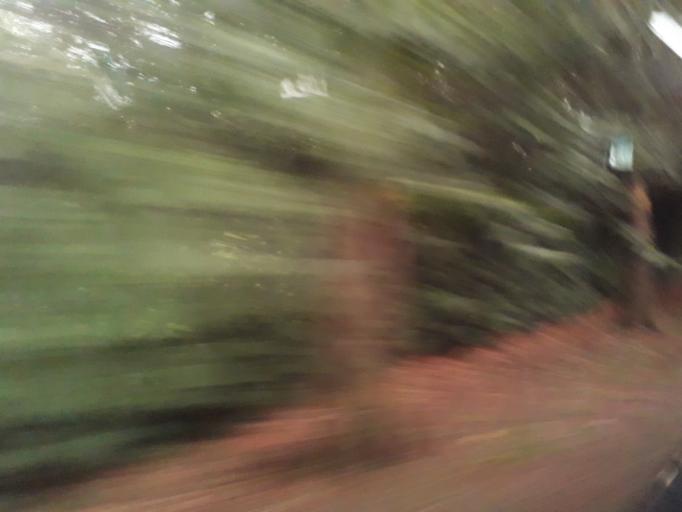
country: MY
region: Perak
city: Ipoh
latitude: 4.5994
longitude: 101.1106
